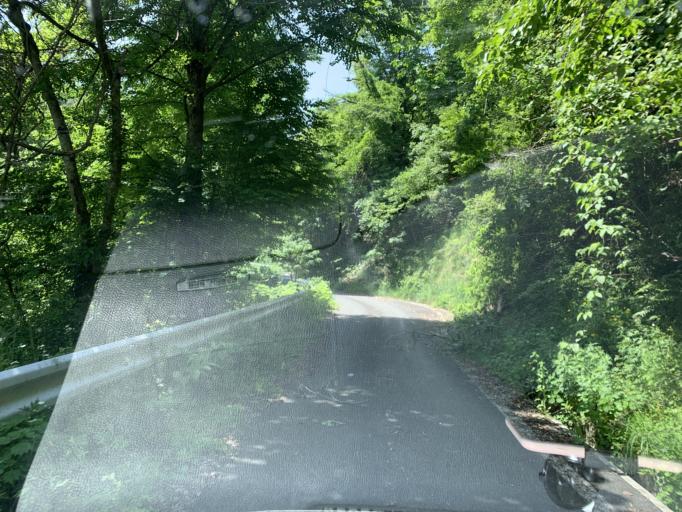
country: JP
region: Iwate
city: Ichinoseki
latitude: 38.9574
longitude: 141.2427
